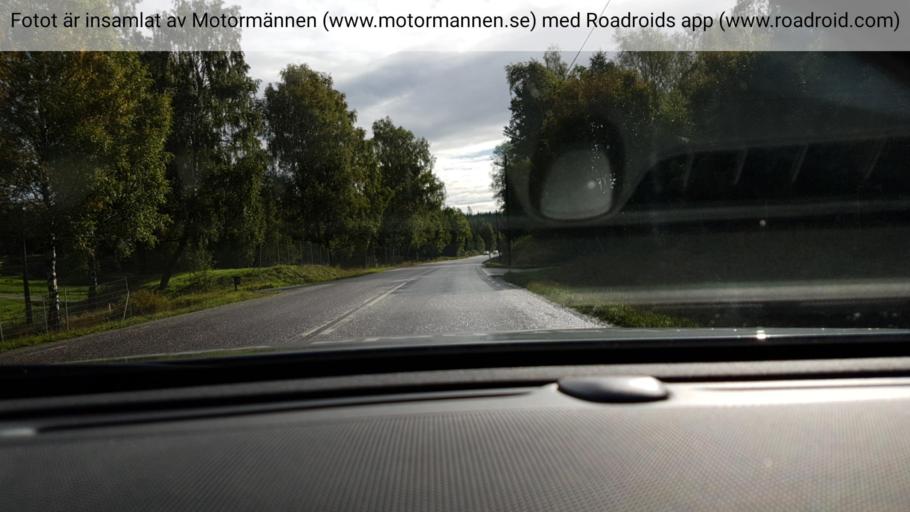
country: SE
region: Vaestra Goetaland
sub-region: Marks Kommun
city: Bua
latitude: 57.5075
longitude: 12.6000
